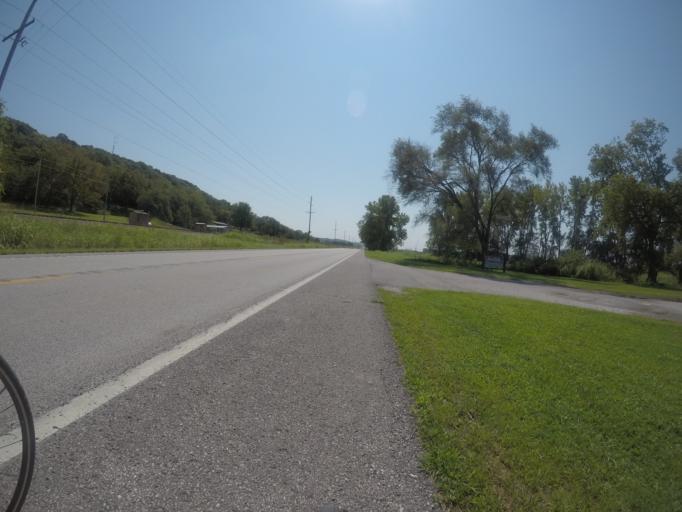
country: US
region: Kansas
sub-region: Atchison County
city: Atchison
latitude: 39.5308
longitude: -95.0356
